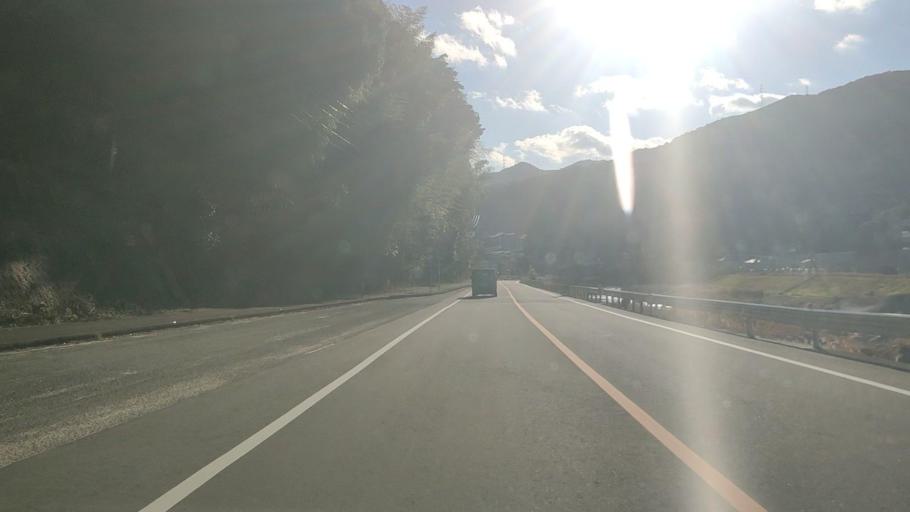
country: JP
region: Saga Prefecture
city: Saga-shi
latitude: 33.3571
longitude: 130.2519
